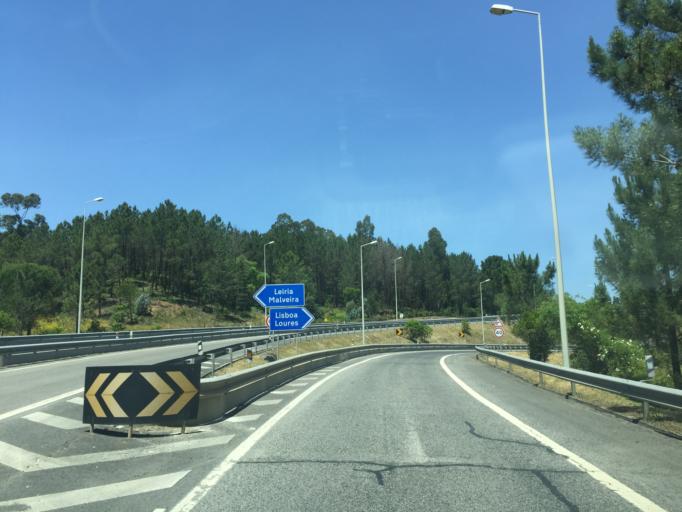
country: PT
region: Lisbon
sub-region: Mafra
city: Venda do Pinheiro
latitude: 38.9057
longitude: -9.2067
